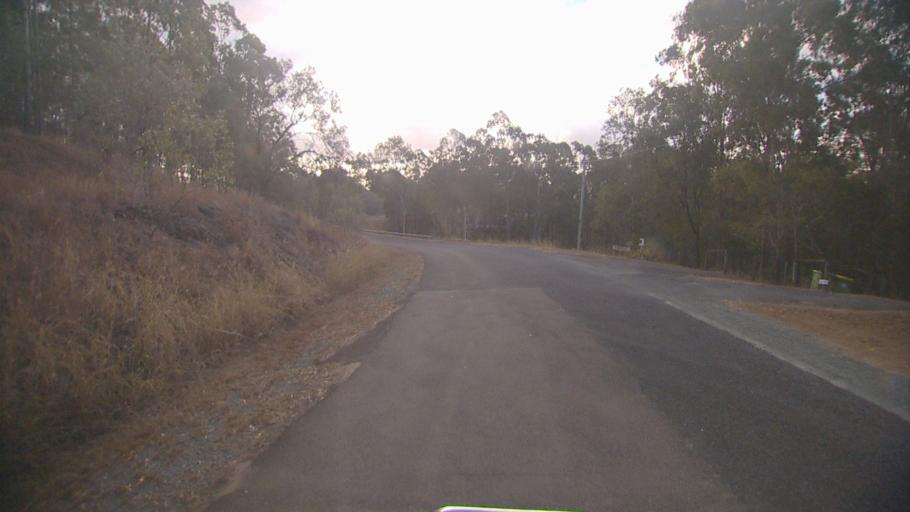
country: AU
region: Queensland
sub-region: Logan
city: Cedar Vale
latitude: -27.9016
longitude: 153.0739
